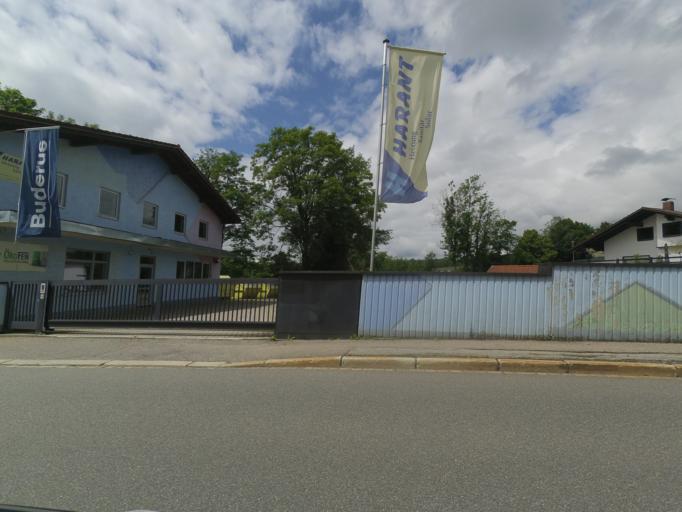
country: DE
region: Bavaria
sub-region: Lower Bavaria
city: Zwiesel
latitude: 49.0252
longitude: 13.2316
